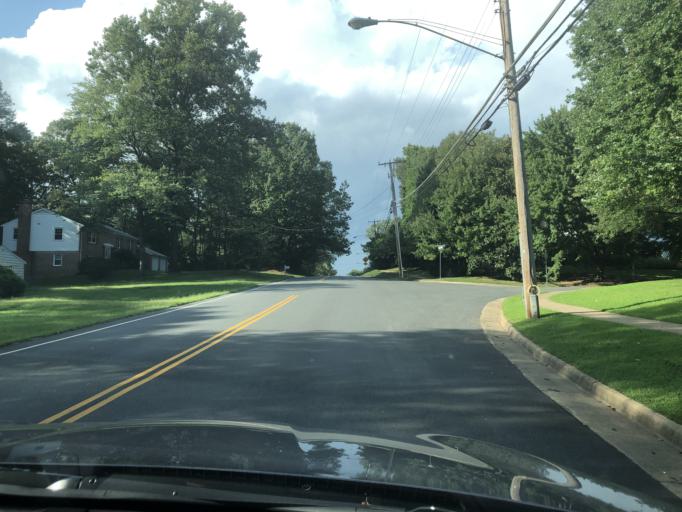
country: US
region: Virginia
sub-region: City of Fairfax
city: Fairfax
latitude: 38.8388
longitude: -77.2882
